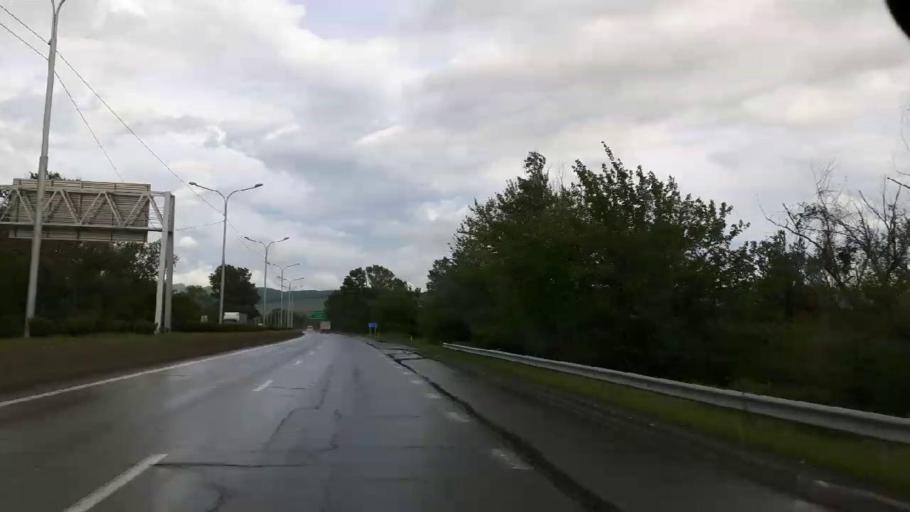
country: GE
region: Shida Kartli
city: Kaspi
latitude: 41.9127
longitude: 44.5620
